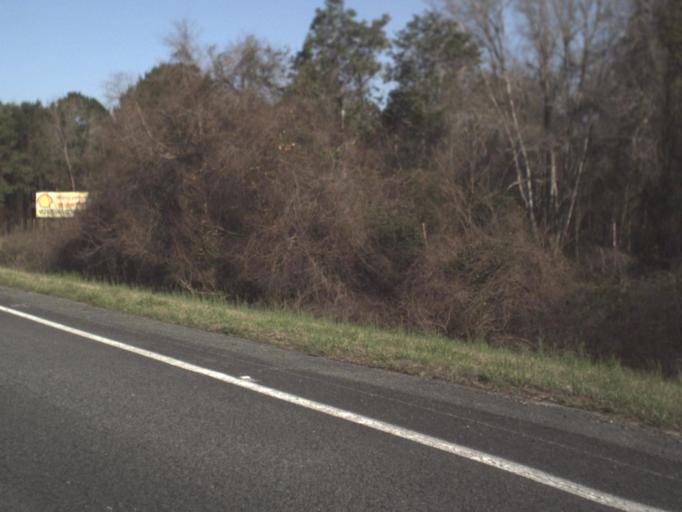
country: US
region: Florida
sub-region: Jefferson County
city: Monticello
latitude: 30.4534
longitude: -83.7578
